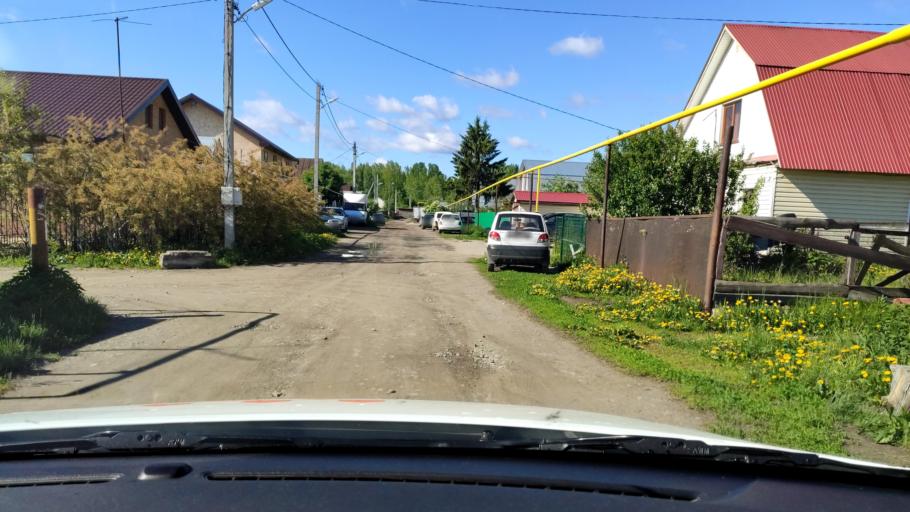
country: RU
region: Tatarstan
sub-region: Gorod Kazan'
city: Kazan
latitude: 55.7368
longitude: 49.0911
